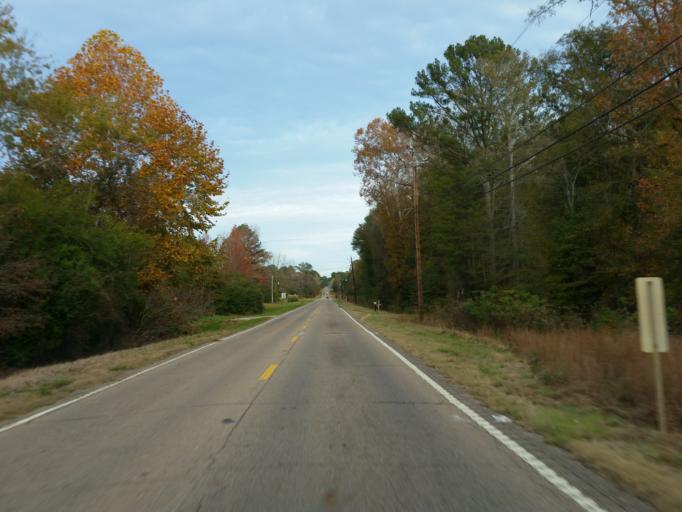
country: US
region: Mississippi
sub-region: Lauderdale County
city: Marion
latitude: 32.4053
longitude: -88.5895
